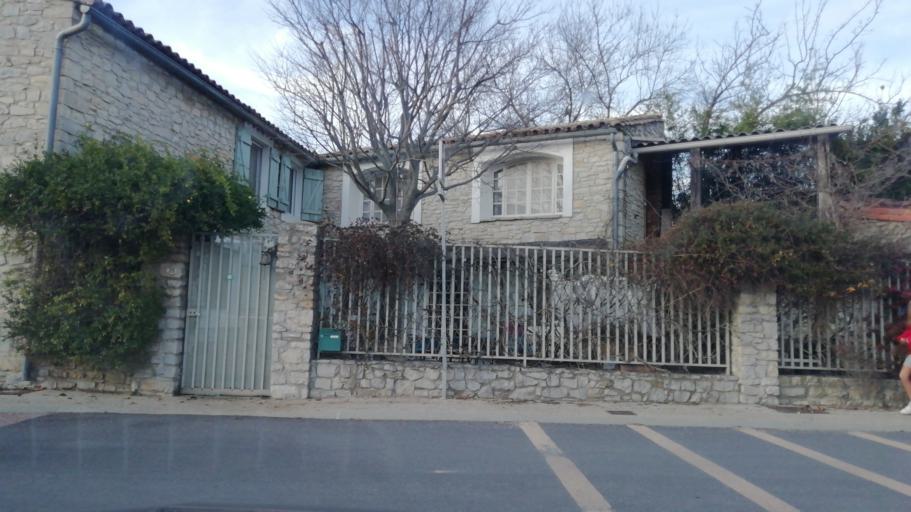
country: FR
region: Languedoc-Roussillon
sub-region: Departement de l'Herault
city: Claret
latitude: 43.8437
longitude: 3.9424
